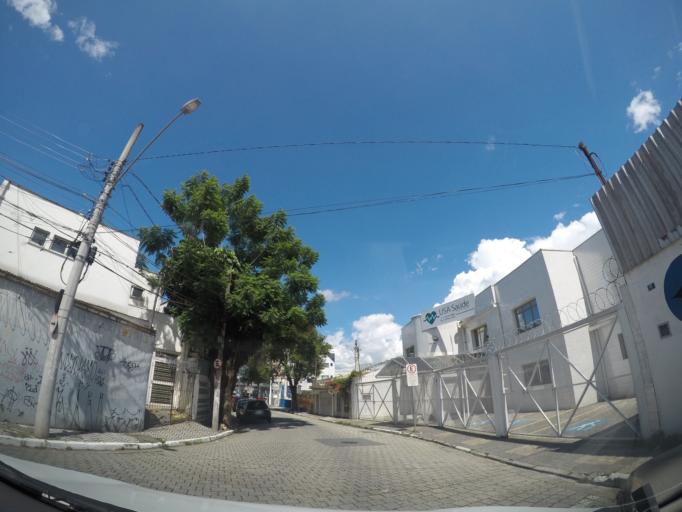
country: BR
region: Sao Paulo
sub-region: Guarulhos
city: Guarulhos
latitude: -23.4625
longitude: -46.5338
